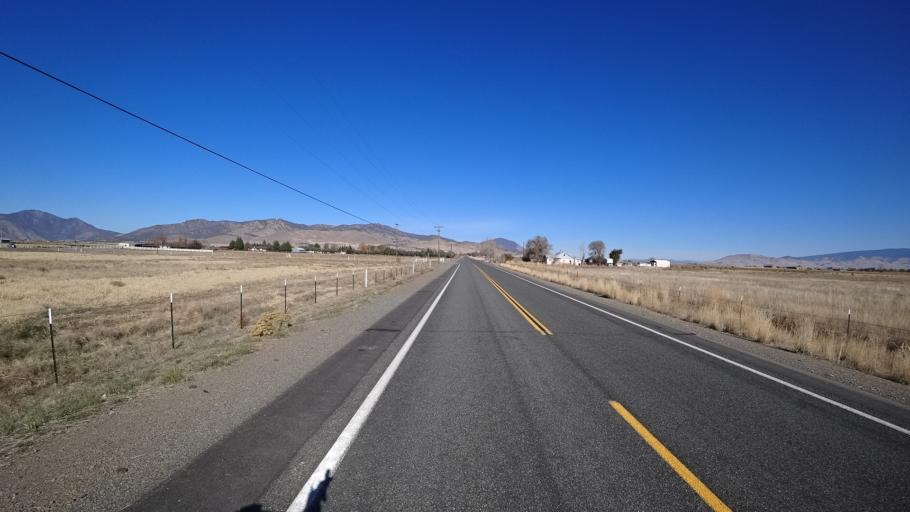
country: US
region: California
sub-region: Siskiyou County
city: Montague
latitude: 41.7483
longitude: -122.5247
